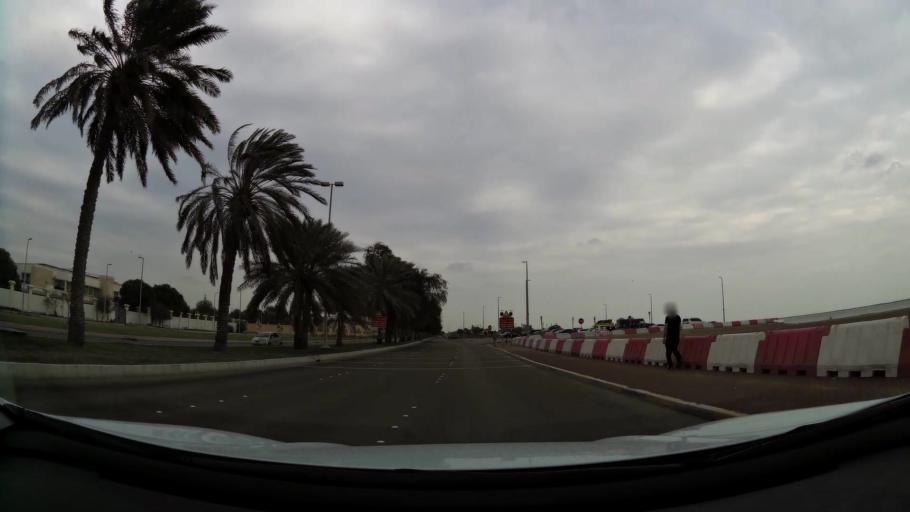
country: AE
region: Abu Dhabi
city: Abu Dhabi
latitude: 24.4298
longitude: 54.3727
